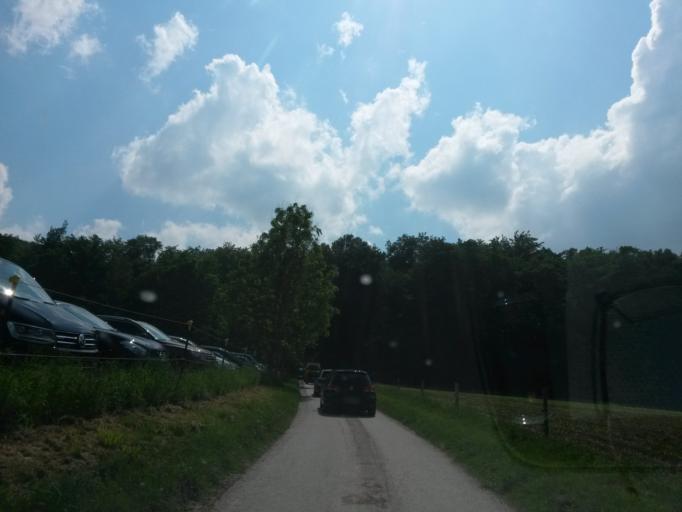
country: DE
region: North Rhine-Westphalia
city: Balve
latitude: 51.3395
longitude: 7.8890
